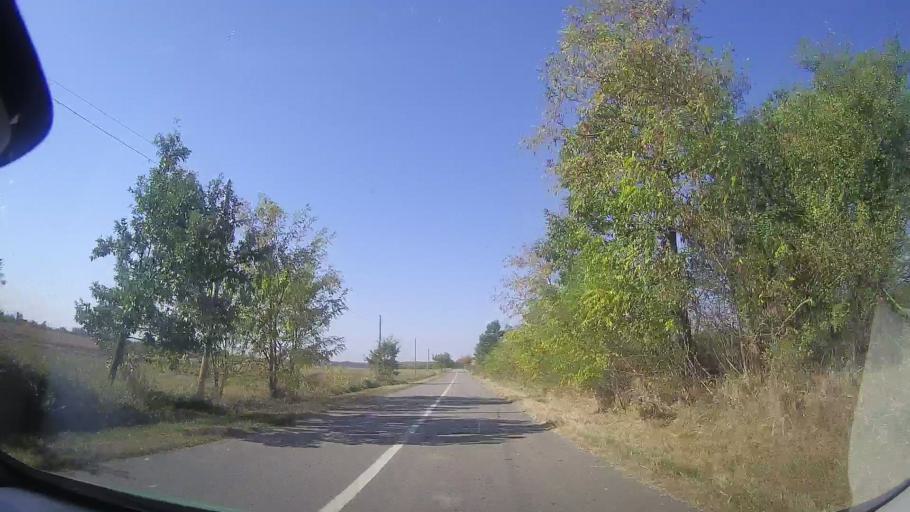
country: RO
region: Timis
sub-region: Comuna Ghizela
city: Ghizela
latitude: 45.8296
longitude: 21.7526
